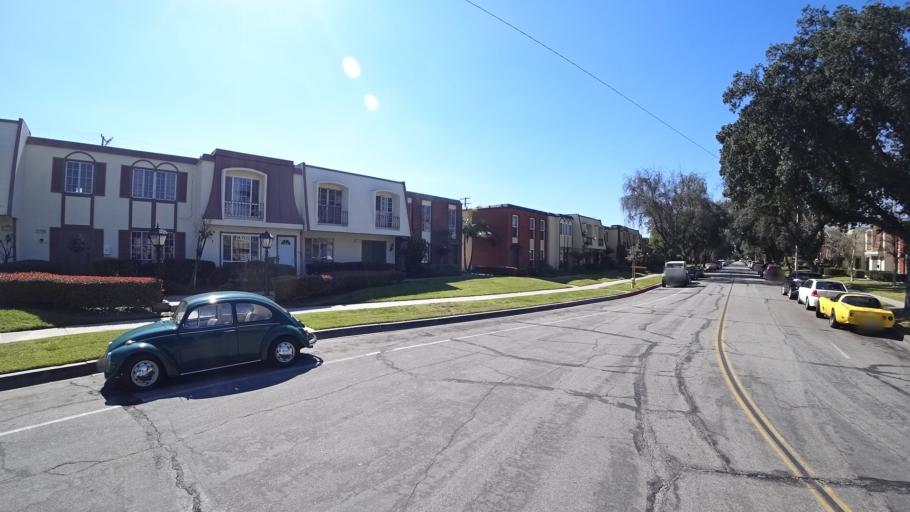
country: US
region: California
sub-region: Orange County
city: Anaheim
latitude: 33.8422
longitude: -117.9435
